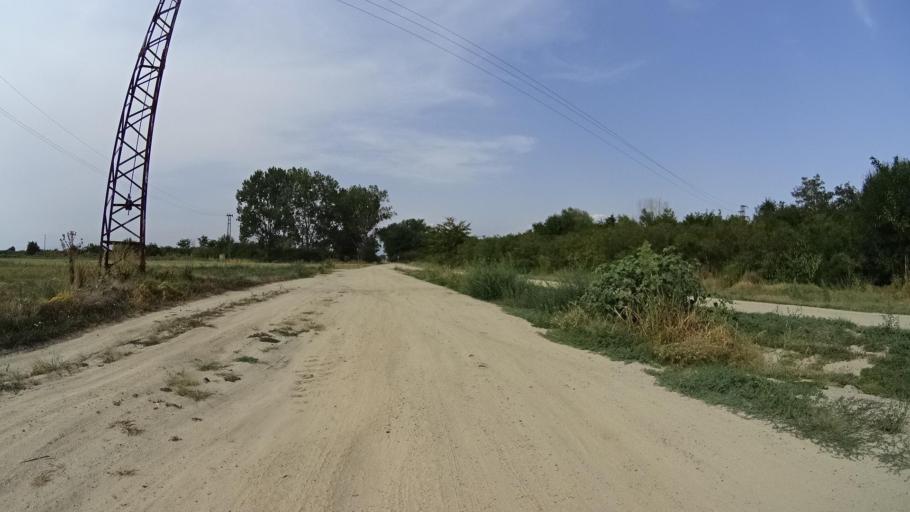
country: BG
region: Plovdiv
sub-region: Obshtina Kaloyanovo
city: Kaloyanovo
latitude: 42.3040
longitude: 24.7992
